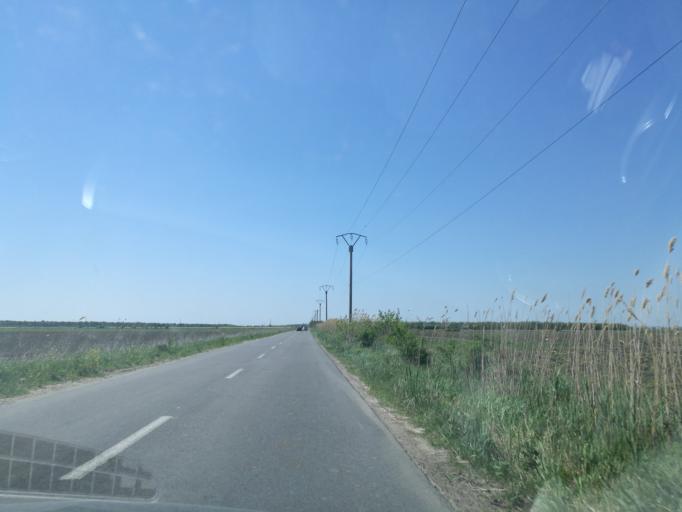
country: RO
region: Prahova
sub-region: Comuna Draganesti
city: Meri
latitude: 44.8483
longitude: 26.3286
